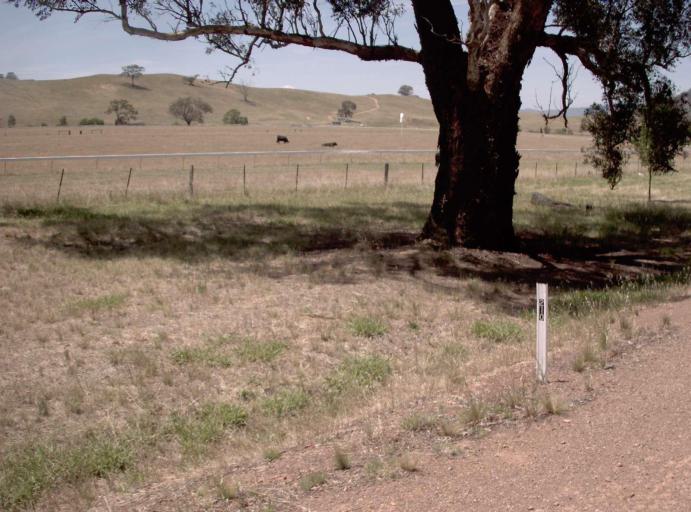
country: AU
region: Victoria
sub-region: East Gippsland
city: Bairnsdale
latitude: -37.2446
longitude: 147.7129
